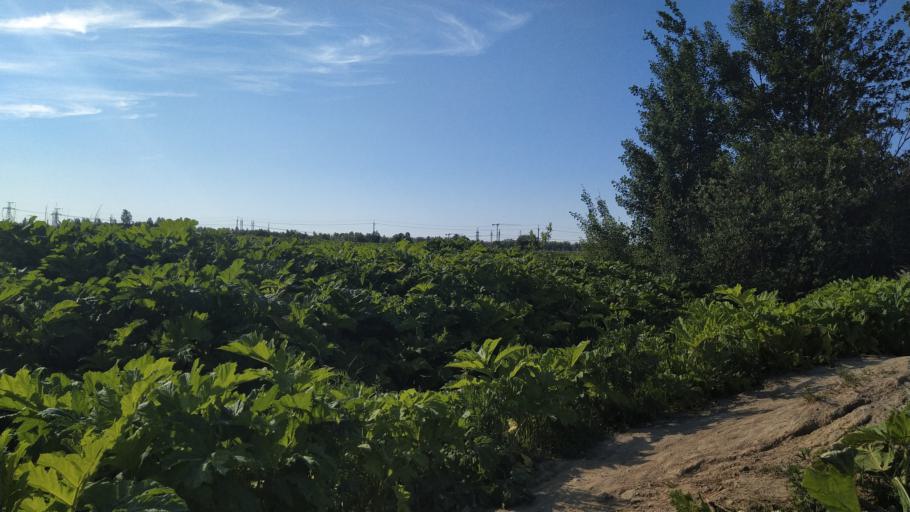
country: RU
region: St.-Petersburg
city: Pushkin
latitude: 59.7416
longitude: 30.3844
